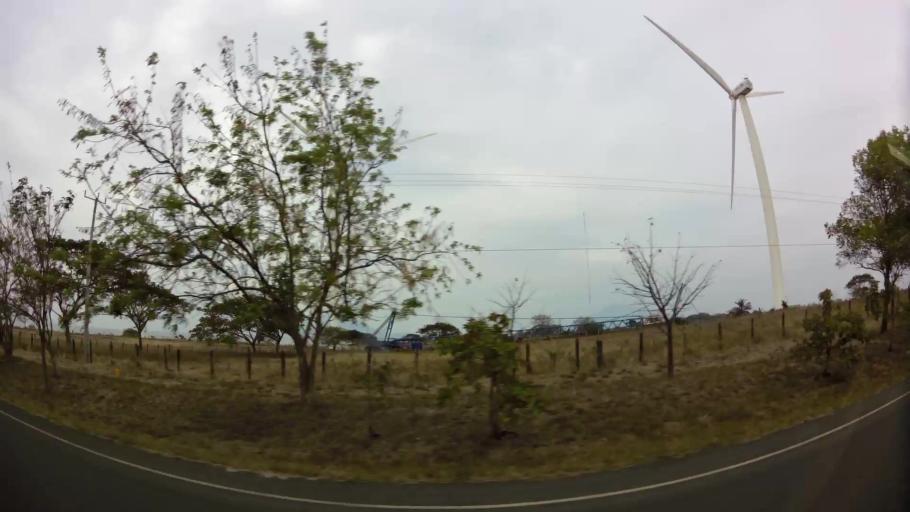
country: NI
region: Rivas
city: Rivas
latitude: 11.3301
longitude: -85.7213
